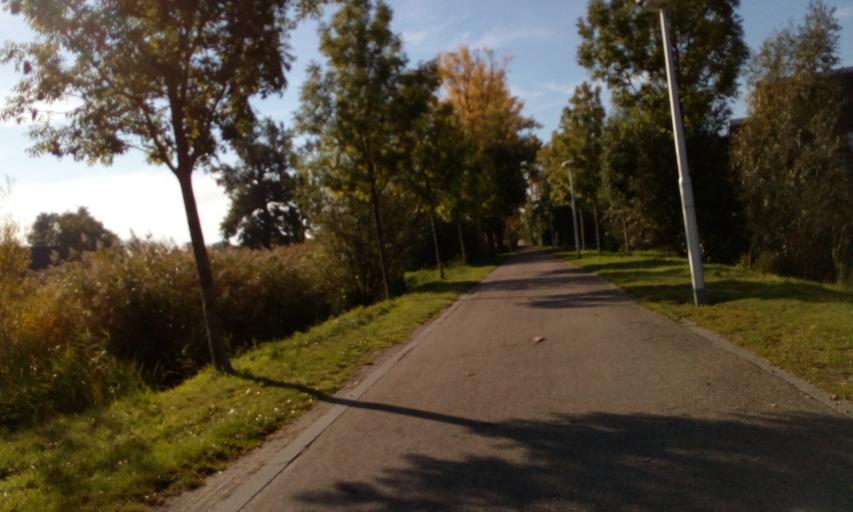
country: NL
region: Utrecht
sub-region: Stichtse Vecht
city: Maarssen
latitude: 52.1087
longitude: 5.0337
